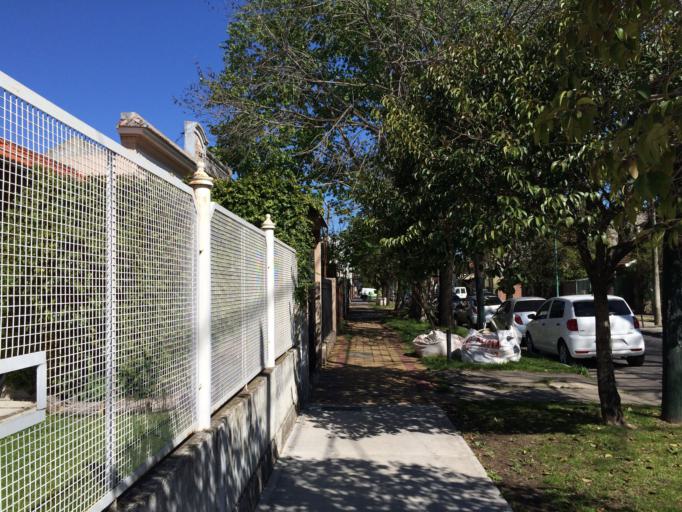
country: AR
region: Buenos Aires
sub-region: Partido de Lomas de Zamora
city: Lomas de Zamora
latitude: -34.7544
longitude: -58.3938
